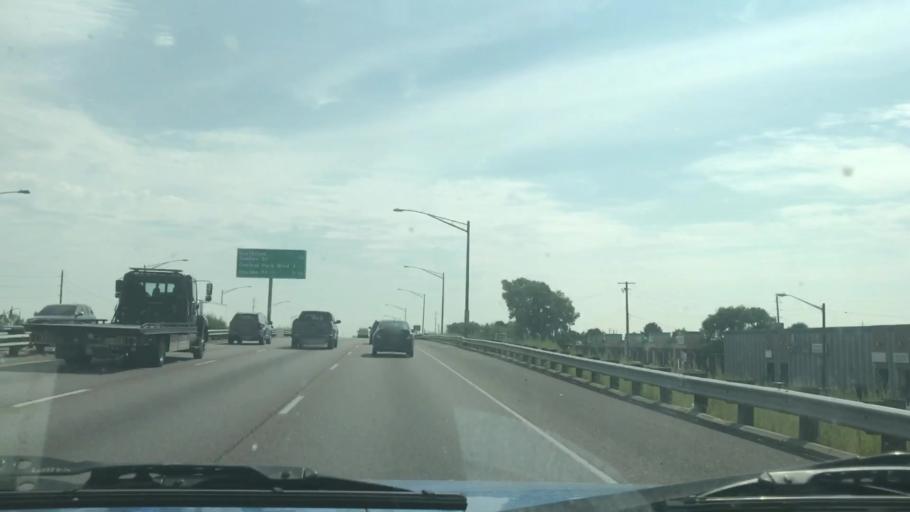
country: US
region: Colorado
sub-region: Adams County
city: Commerce City
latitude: 39.7782
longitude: -104.9148
